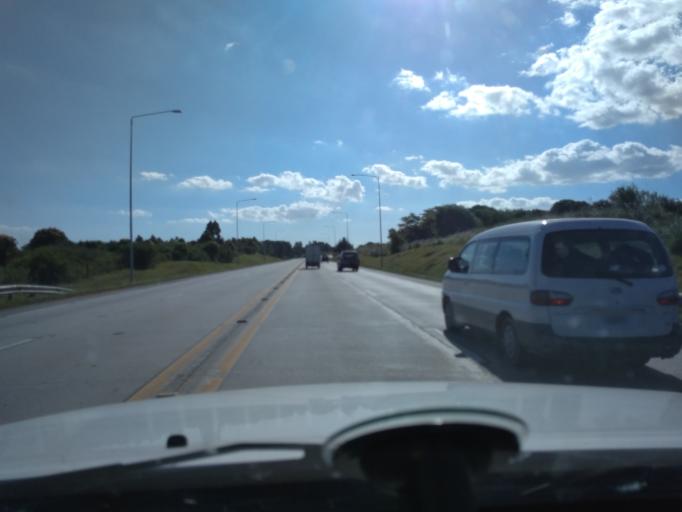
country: UY
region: Canelones
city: La Paz
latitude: -34.7818
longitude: -56.2427
